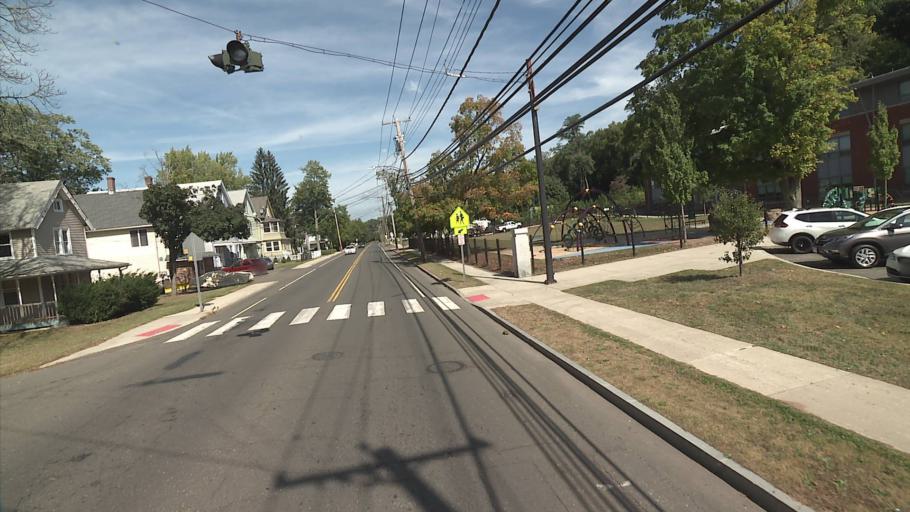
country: US
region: Connecticut
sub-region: New Haven County
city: East Haven
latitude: 41.3272
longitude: -72.8700
